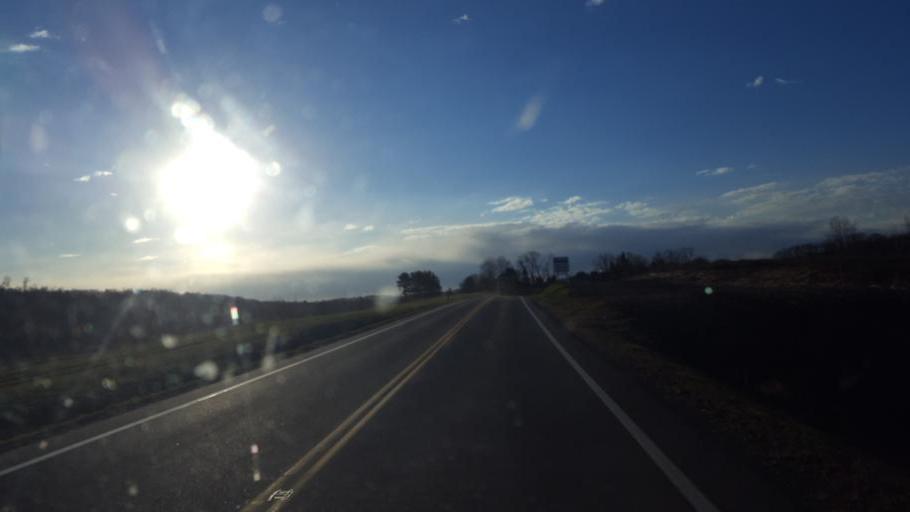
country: US
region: Ohio
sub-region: Ashland County
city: Loudonville
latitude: 40.6517
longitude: -82.2562
